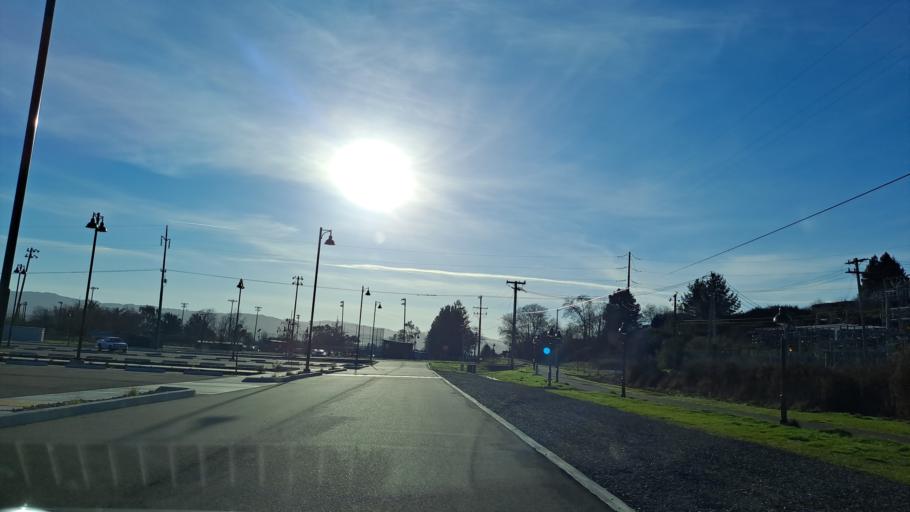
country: US
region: California
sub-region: Humboldt County
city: Fortuna
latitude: 40.5946
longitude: -124.1341
